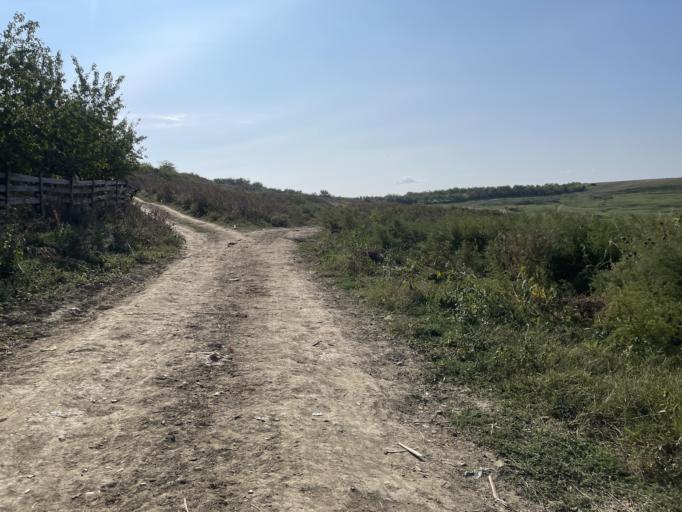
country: RO
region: Iasi
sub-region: Comuna Dumesti
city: Pausesti
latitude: 47.1536
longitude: 27.3155
